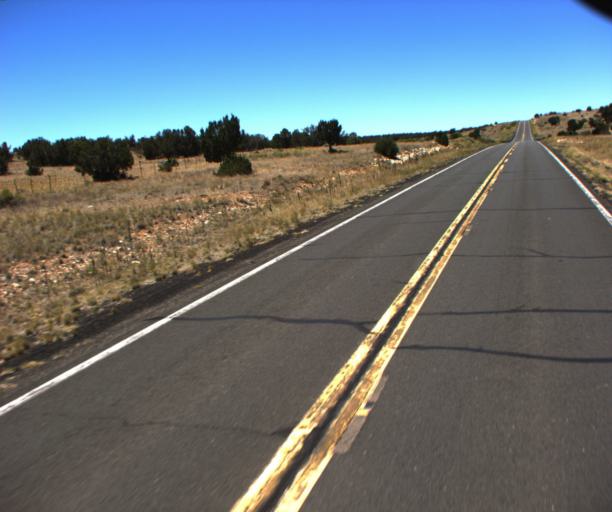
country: US
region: Arizona
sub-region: Coconino County
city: LeChee
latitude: 34.7673
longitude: -111.0108
